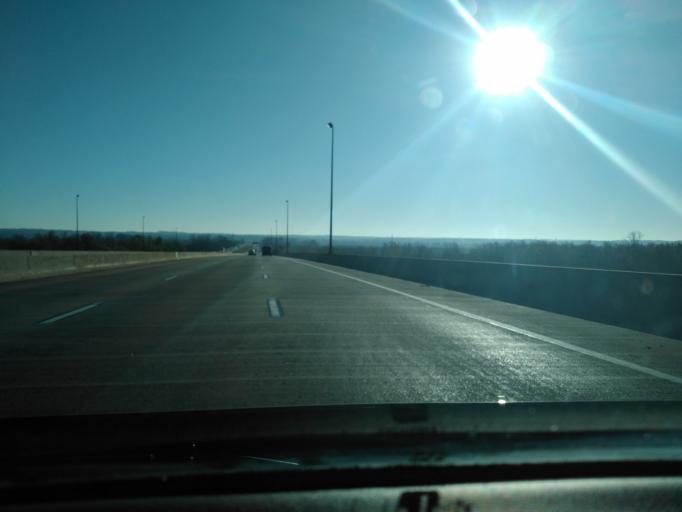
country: US
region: Missouri
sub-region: Saint Louis County
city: Oakville
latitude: 38.4858
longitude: -90.2730
